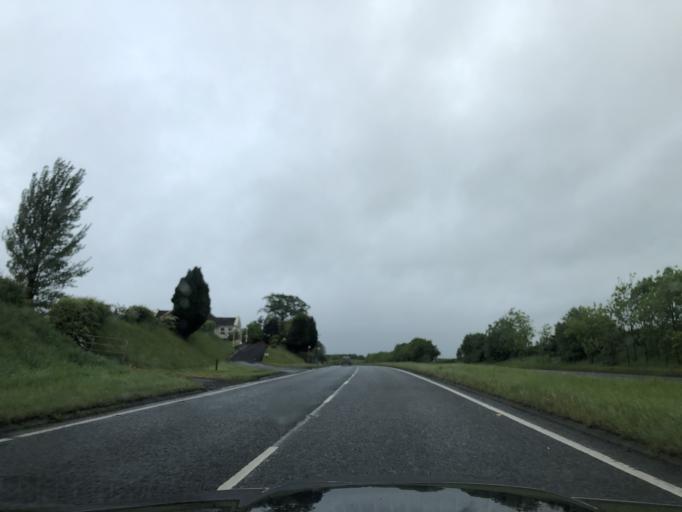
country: GB
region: Northern Ireland
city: Connor
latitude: 54.8025
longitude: -6.2576
